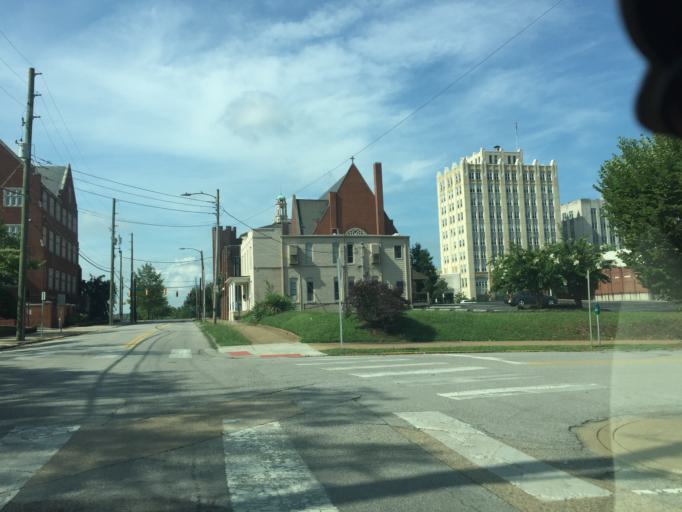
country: US
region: Tennessee
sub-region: Hamilton County
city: Chattanooga
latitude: 35.0470
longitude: -85.3011
